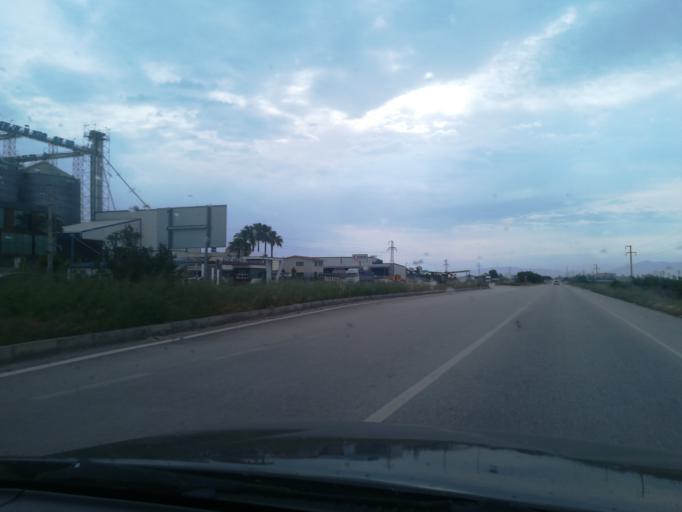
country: TR
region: Adana
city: Yuregir
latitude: 36.9782
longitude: 35.4652
